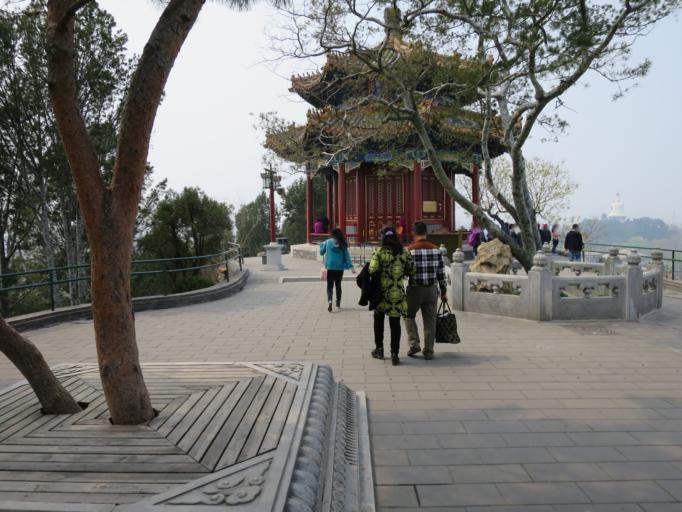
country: CN
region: Beijing
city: Jingshan
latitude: 39.9234
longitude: 116.3898
